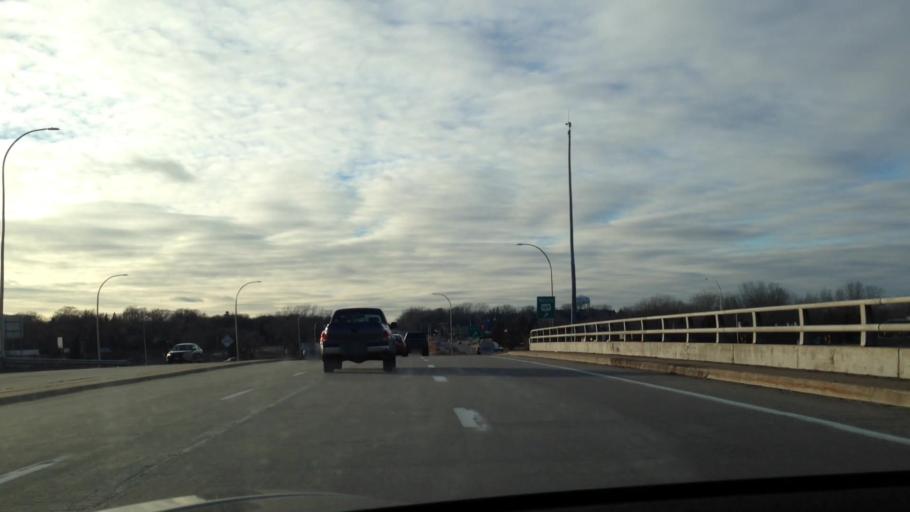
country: US
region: Minnesota
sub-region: Hennepin County
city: New Hope
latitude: 45.0334
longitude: -93.4005
